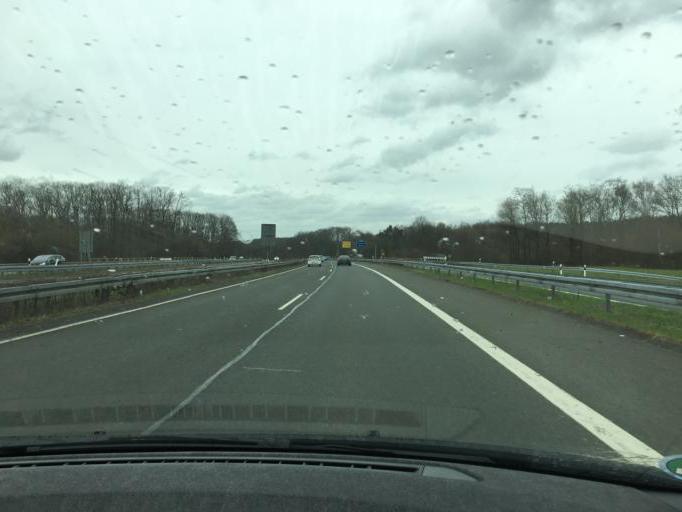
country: DE
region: North Rhine-Westphalia
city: Herdecke
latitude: 51.4422
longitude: 7.4844
